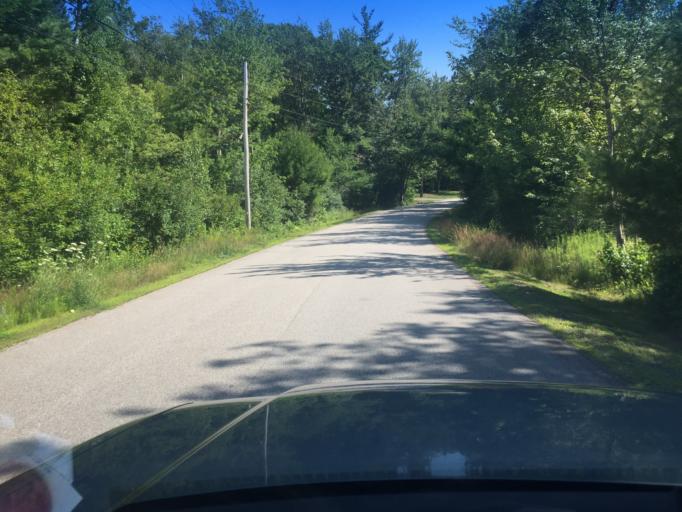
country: US
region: Maine
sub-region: York County
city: York Harbor
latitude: 43.1592
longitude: -70.6439
